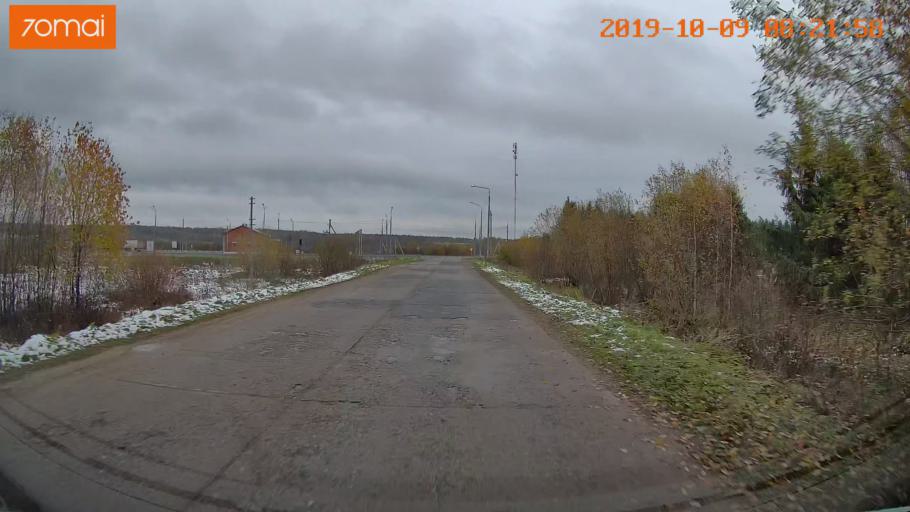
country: RU
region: Vologda
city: Gryazovets
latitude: 58.7418
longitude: 40.2858
